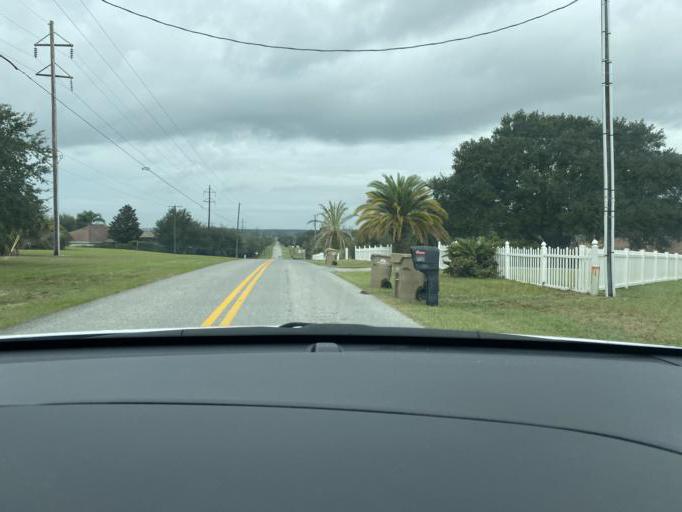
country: US
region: Florida
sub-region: Lake County
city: Minneola
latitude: 28.5948
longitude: -81.7702
